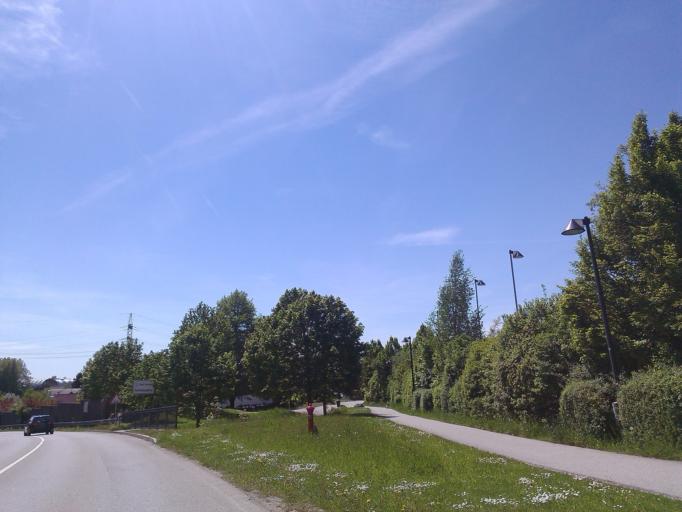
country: DE
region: Bavaria
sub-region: Upper Bavaria
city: Starnberg
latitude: 48.0084
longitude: 11.3481
